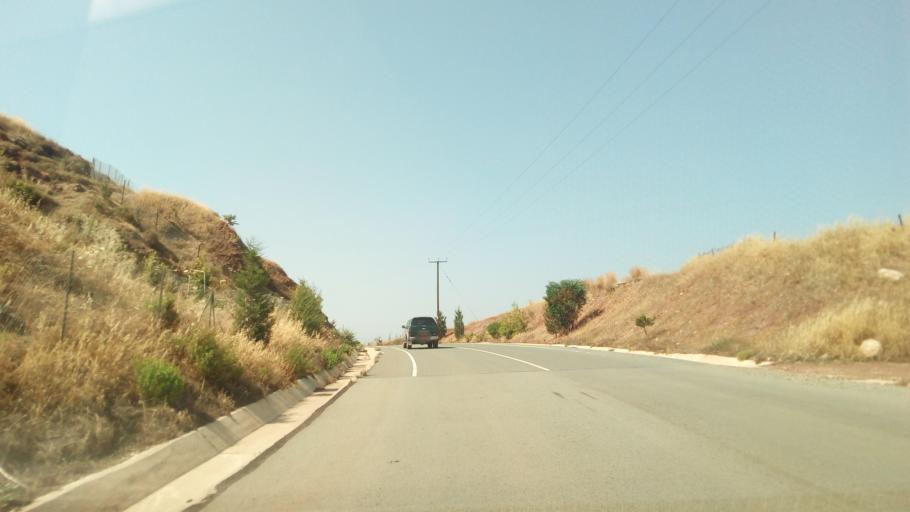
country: CY
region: Limassol
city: Pissouri
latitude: 34.7708
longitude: 32.6029
